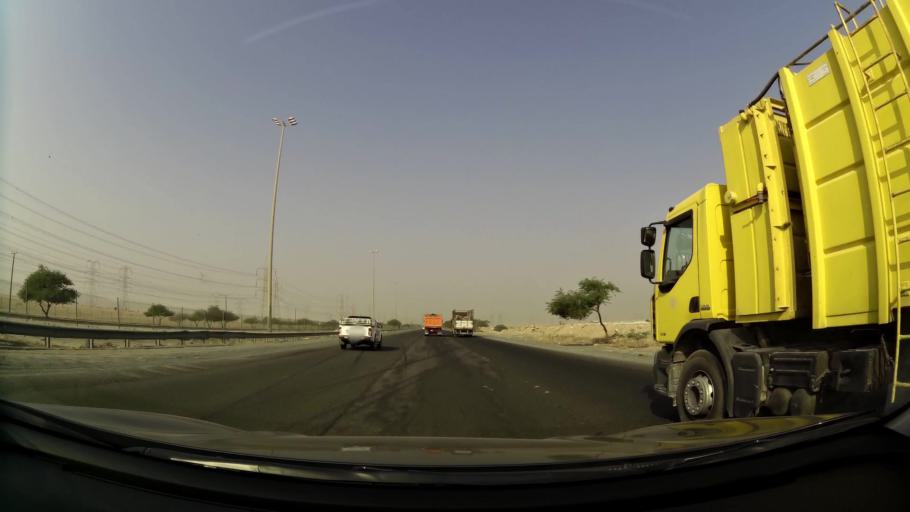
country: KW
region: Al Farwaniyah
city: Al Farwaniyah
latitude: 29.1846
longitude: 47.9024
